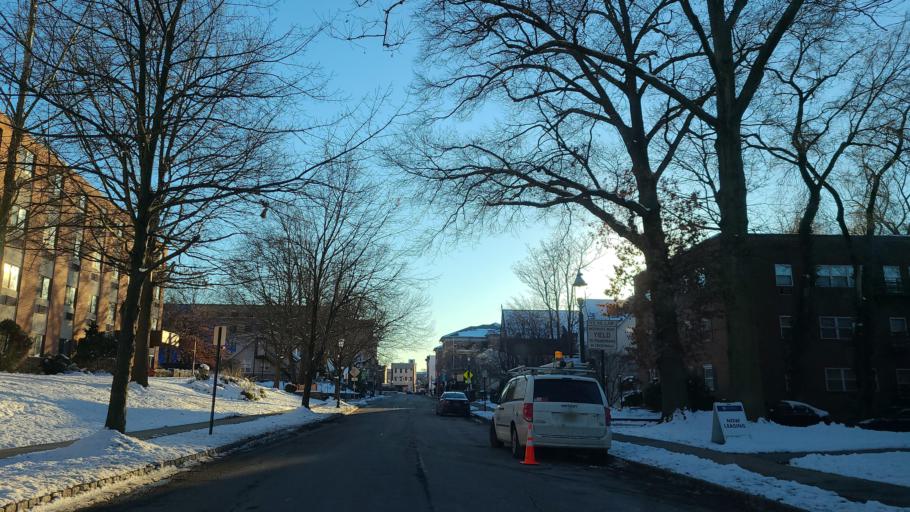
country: US
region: New Jersey
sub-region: Essex County
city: South Orange
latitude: 40.7483
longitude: -74.2575
